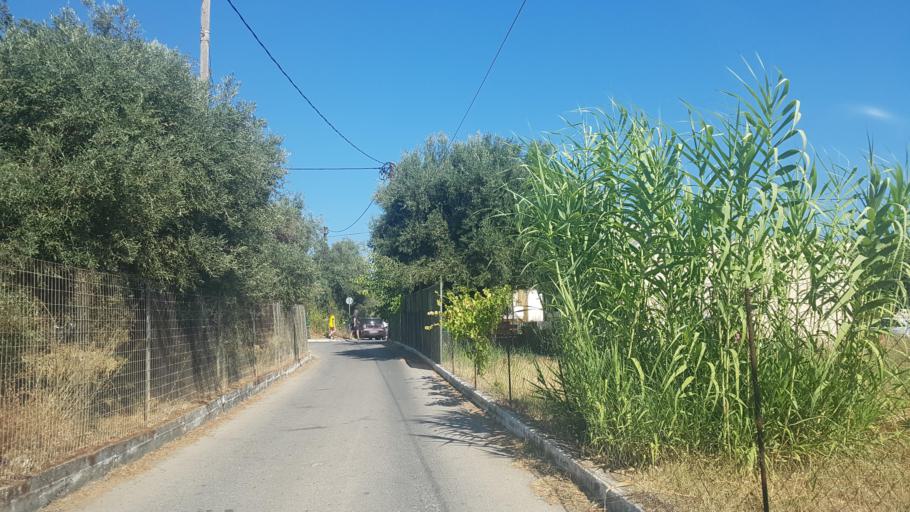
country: GR
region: Crete
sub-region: Nomos Chanias
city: Daratsos
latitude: 35.5102
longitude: 23.9798
